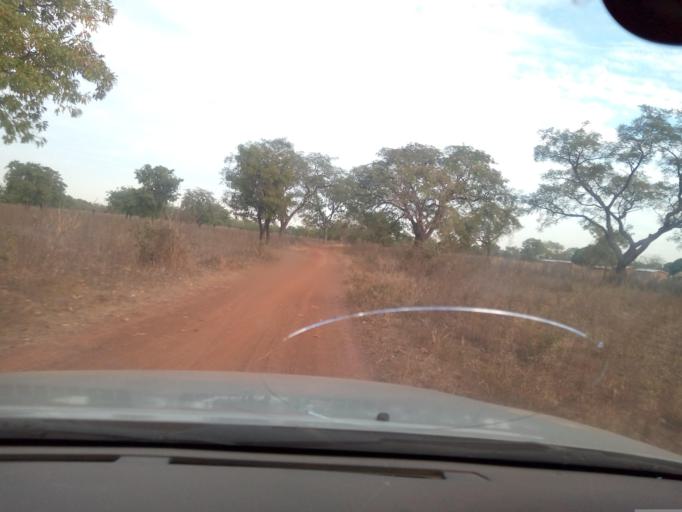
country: ML
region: Sikasso
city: Kadiolo
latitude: 10.5836
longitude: -5.8444
